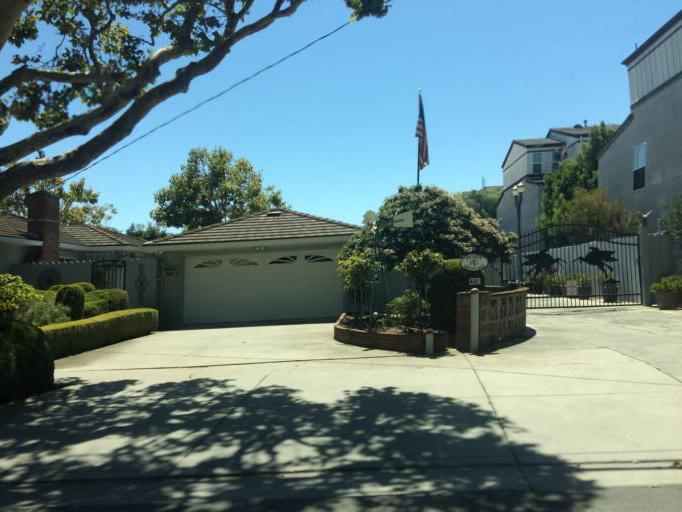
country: US
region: California
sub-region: Santa Clara County
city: San Jose
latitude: 37.3527
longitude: -121.8943
